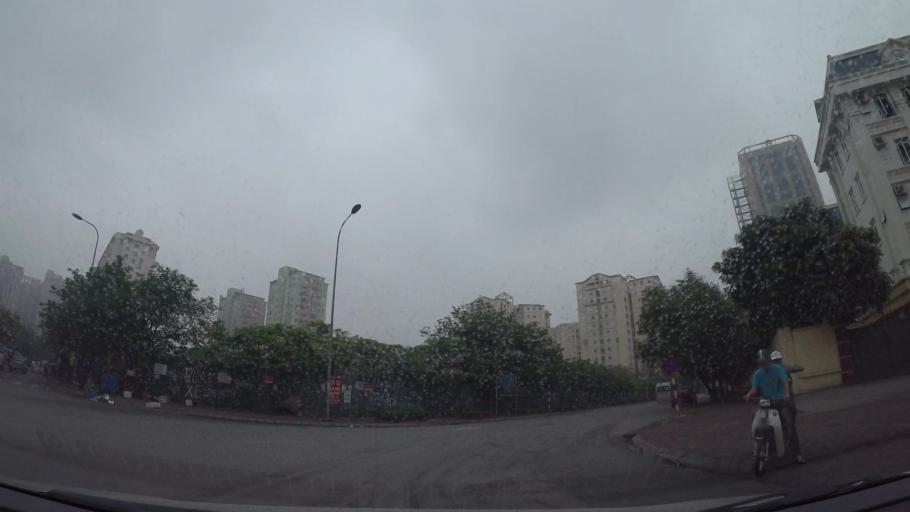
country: VN
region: Ha Noi
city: Thanh Xuan
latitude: 21.0125
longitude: 105.7884
